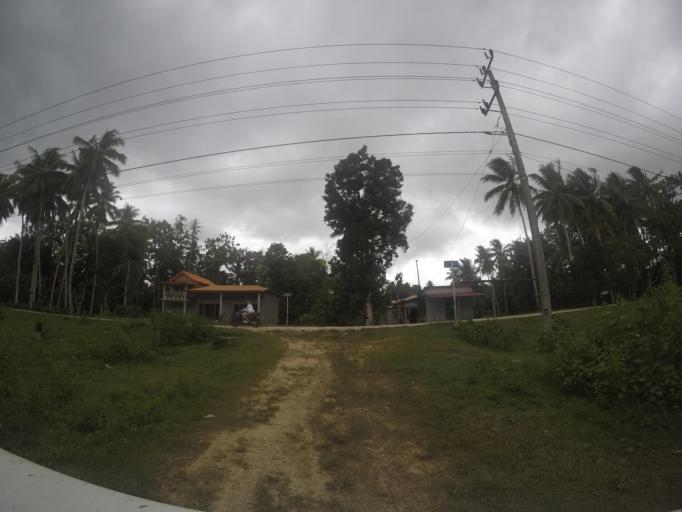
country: TL
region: Lautem
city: Lospalos
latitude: -8.5175
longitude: 126.9910
